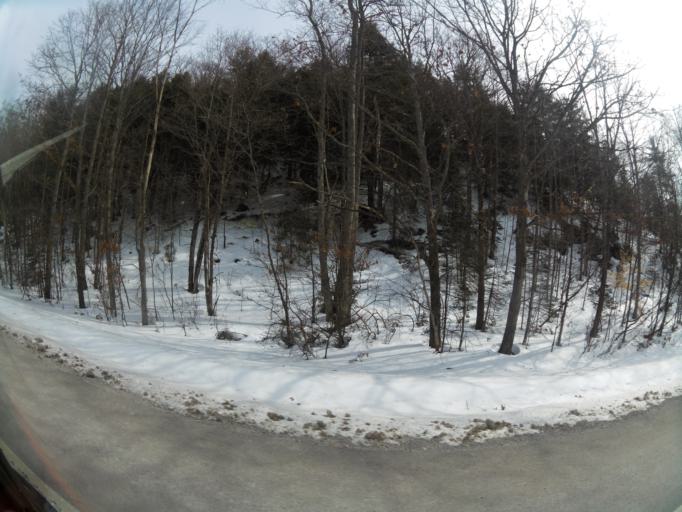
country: CA
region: Quebec
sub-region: Outaouais
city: Maniwaki
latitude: 46.1967
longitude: -75.6744
